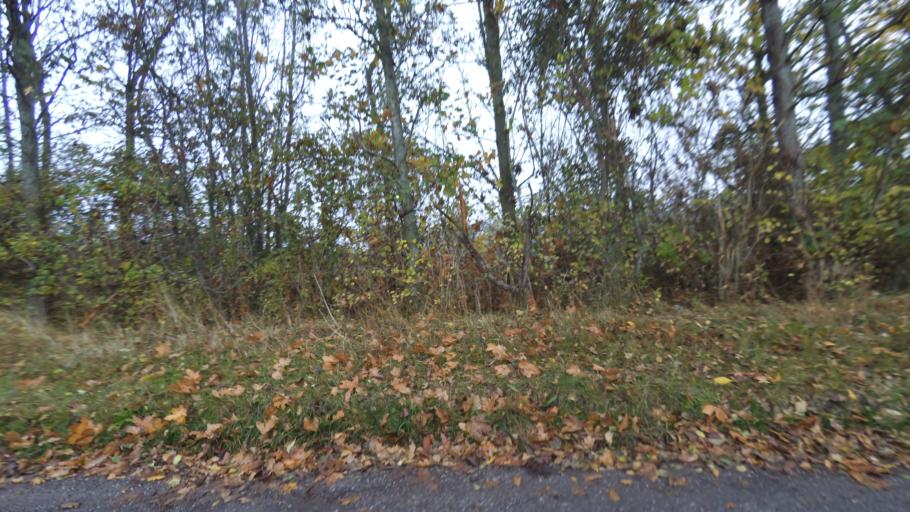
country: DK
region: Central Jutland
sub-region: Odder Kommune
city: Odder
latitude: 55.9277
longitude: 10.2536
